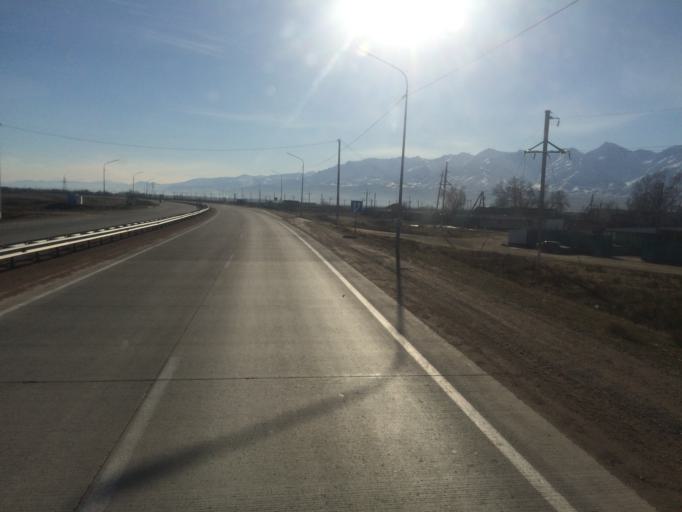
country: KG
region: Talas
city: Ivanovo-Alekseyevka
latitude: 42.9920
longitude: 72.1127
